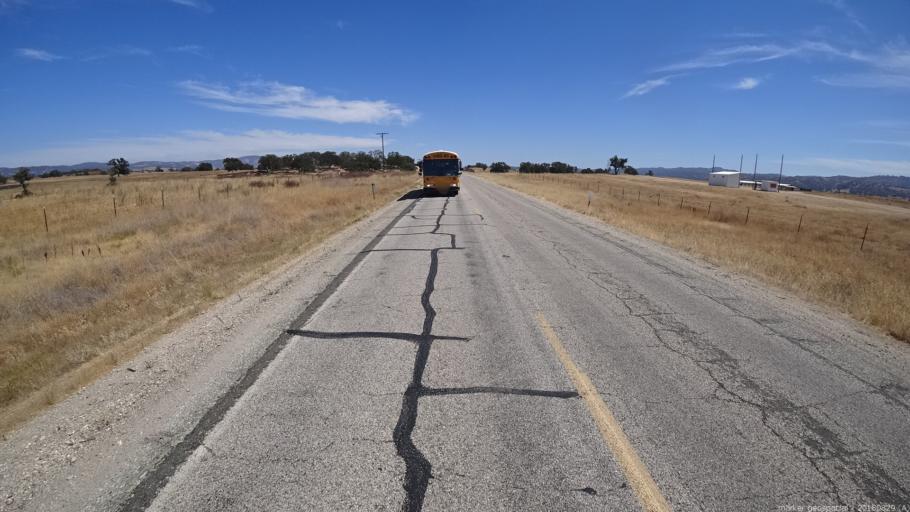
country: US
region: California
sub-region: Monterey County
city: King City
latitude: 35.9609
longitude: -121.1627
